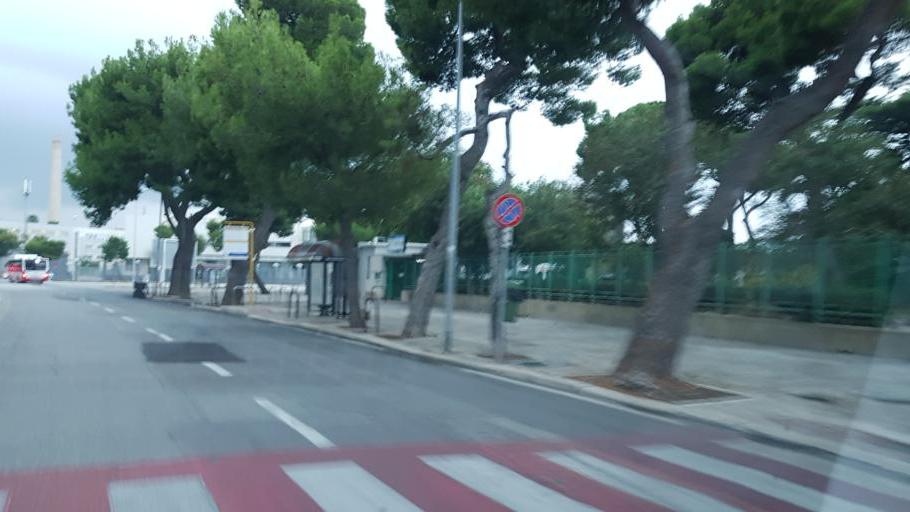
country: IT
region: Apulia
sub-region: Provincia di Bari
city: Bari
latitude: 41.1360
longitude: 16.8445
